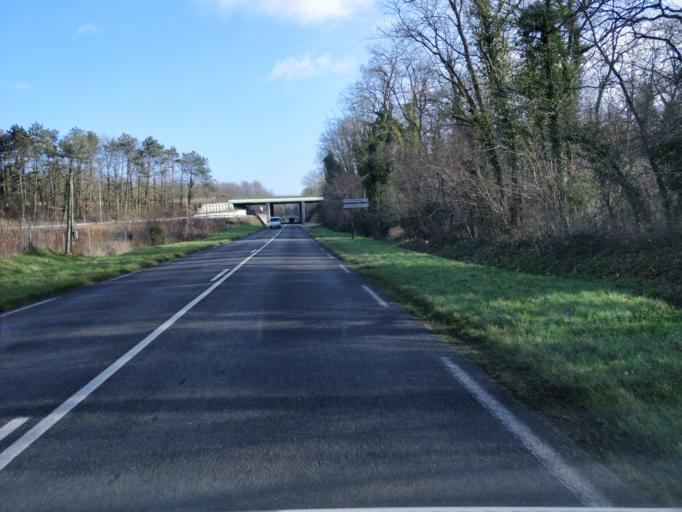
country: FR
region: Ile-de-France
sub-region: Departement de Seine-et-Marne
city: Bagneaux-sur-Loing
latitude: 48.2597
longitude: 2.7228
